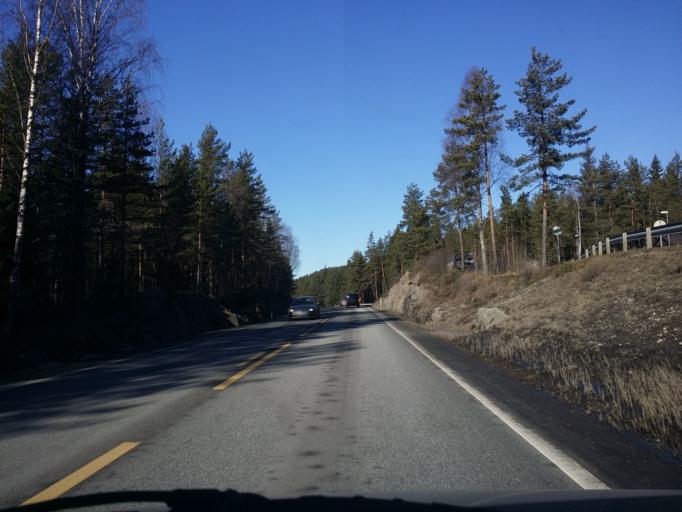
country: NO
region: Buskerud
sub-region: Ringerike
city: Honefoss
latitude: 60.2310
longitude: 10.2347
